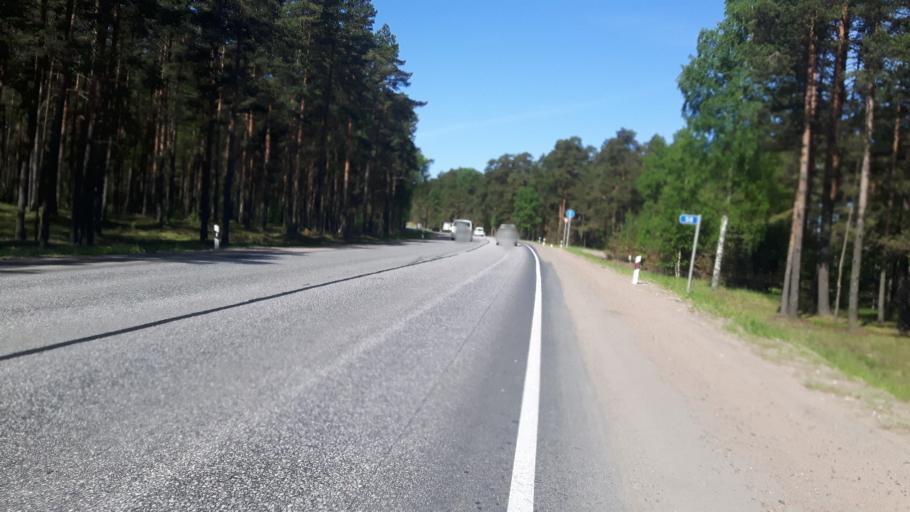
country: RU
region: Leningrad
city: Lebyazh'ye
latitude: 59.9568
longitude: 29.4667
